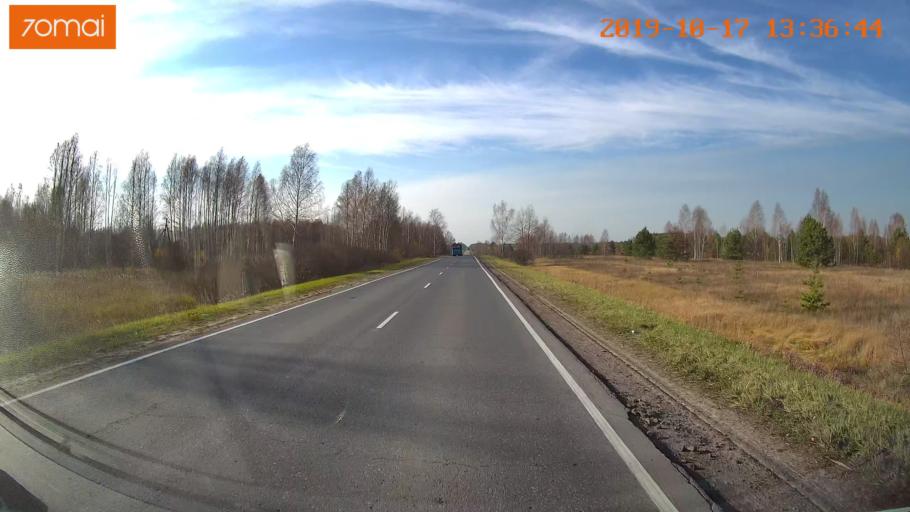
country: RU
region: Rjazan
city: Tuma
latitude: 55.1400
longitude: 40.6566
